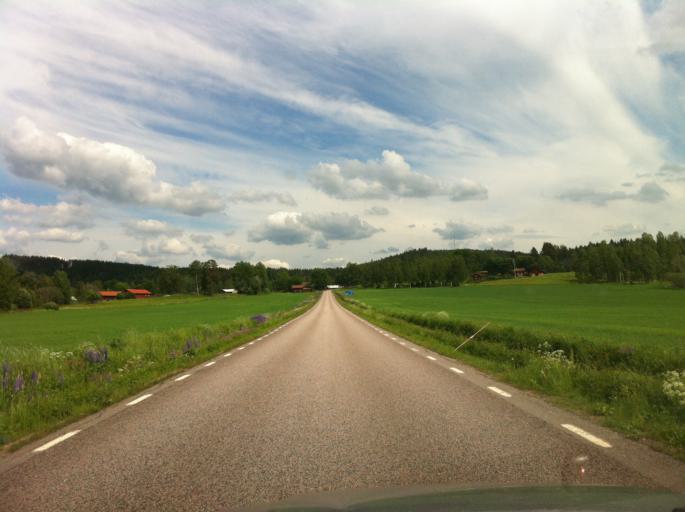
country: SE
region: Vaermland
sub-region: Sunne Kommun
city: Sunne
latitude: 59.7569
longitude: 13.2285
